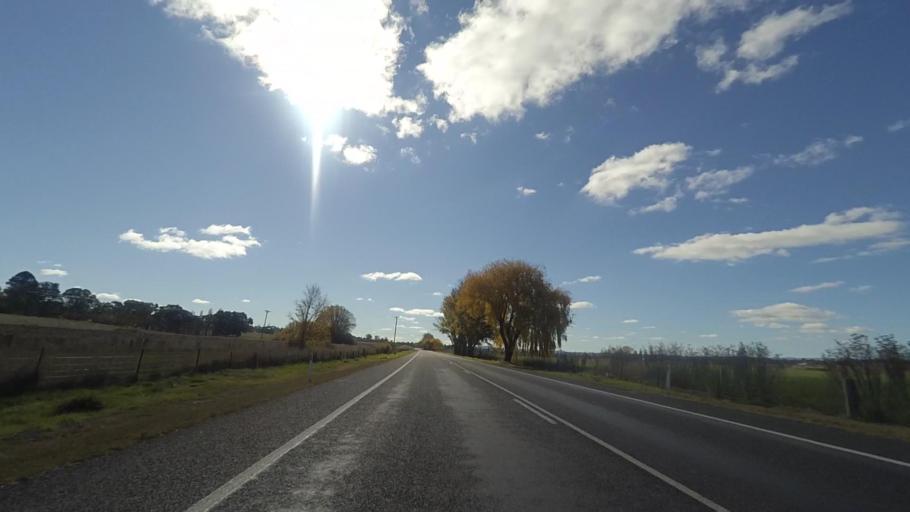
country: AU
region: New South Wales
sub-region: Bathurst Regional
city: Bathurst
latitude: -33.4502
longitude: 149.5789
